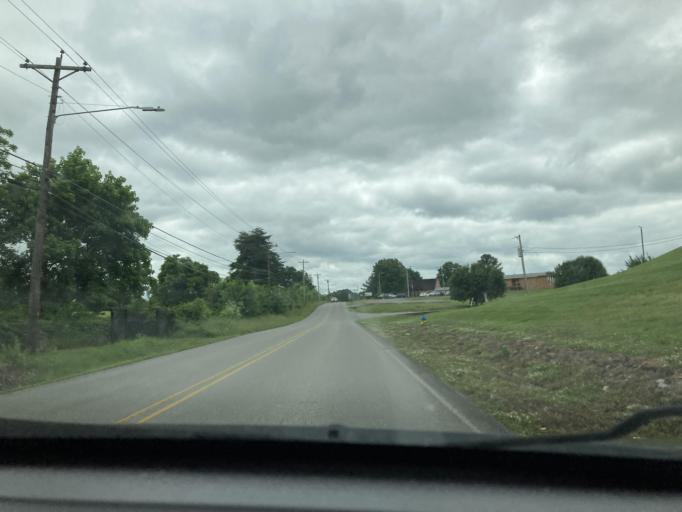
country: US
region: Tennessee
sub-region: Dickson County
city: Dickson
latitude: 36.0890
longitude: -87.3802
